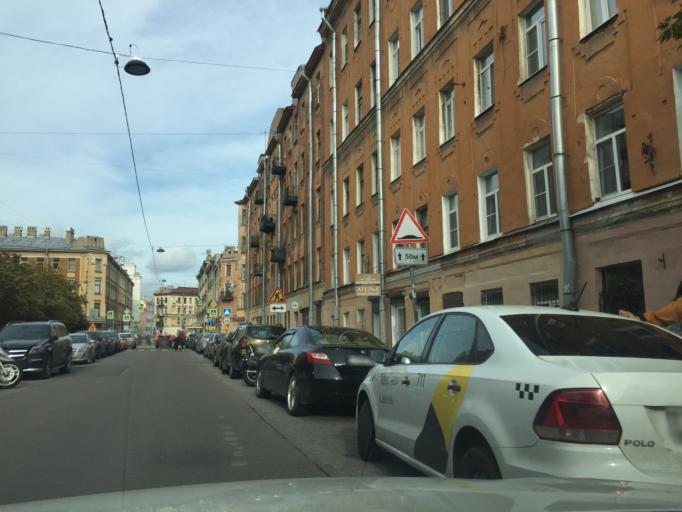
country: RU
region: St.-Petersburg
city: Centralniy
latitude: 59.9361
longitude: 30.3761
